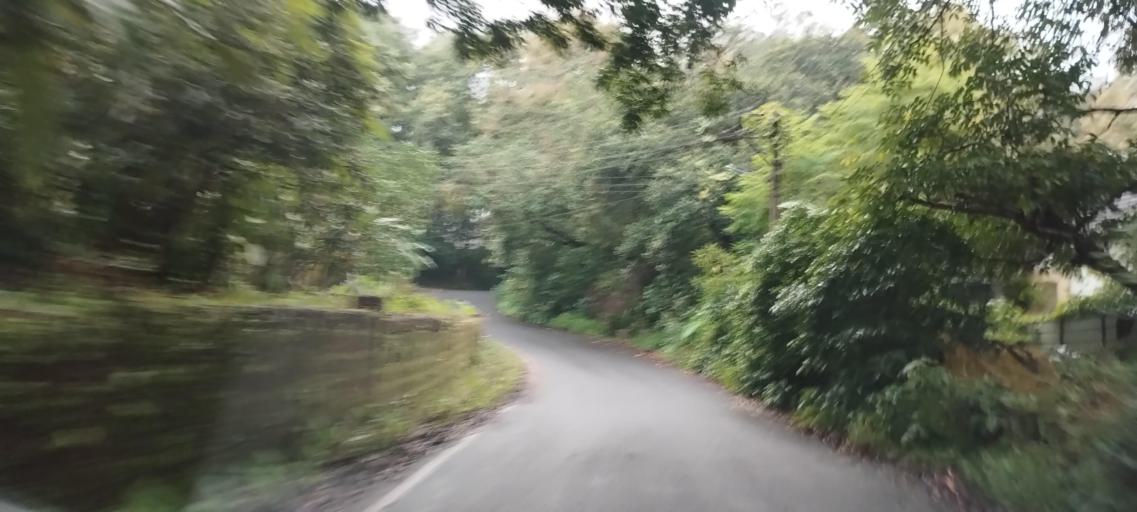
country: IN
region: Goa
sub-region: North Goa
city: Jua
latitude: 15.5206
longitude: 73.8967
